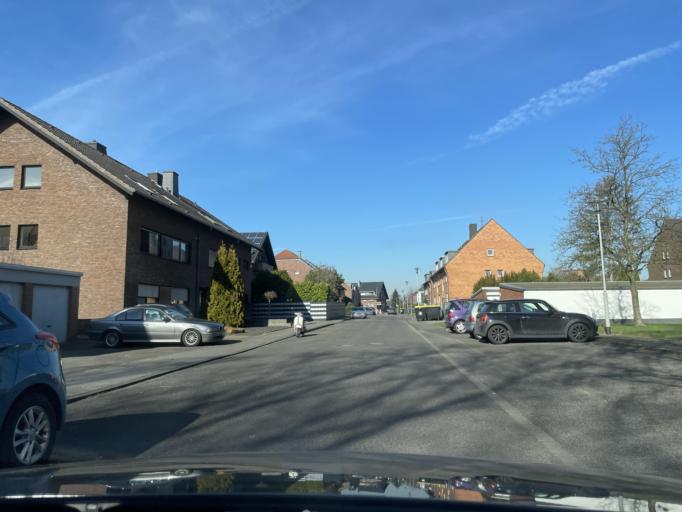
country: DE
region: North Rhine-Westphalia
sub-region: Regierungsbezirk Dusseldorf
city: Monchengladbach
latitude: 51.1985
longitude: 6.3940
